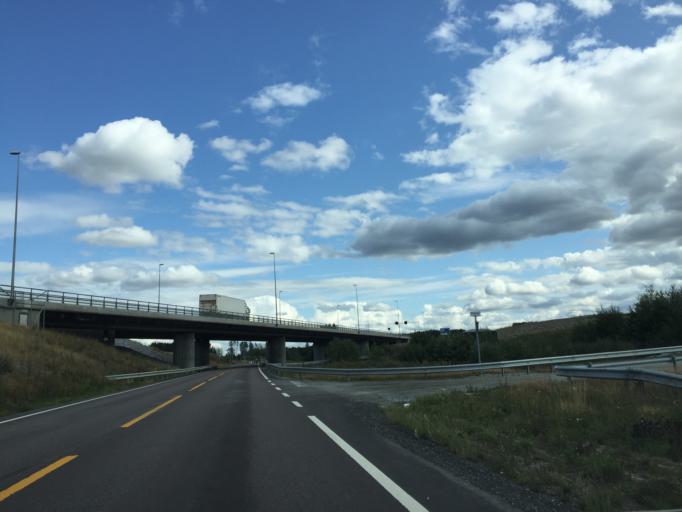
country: NO
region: Ostfold
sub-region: Hobol
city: Tomter
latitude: 59.6224
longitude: 10.9950
